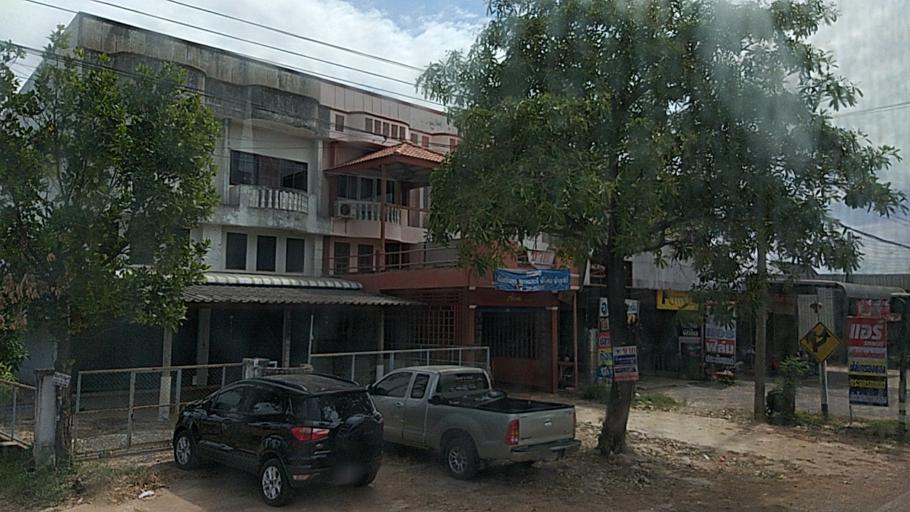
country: TH
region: Maha Sarakham
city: Chiang Yuen
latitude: 16.4014
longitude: 103.0997
